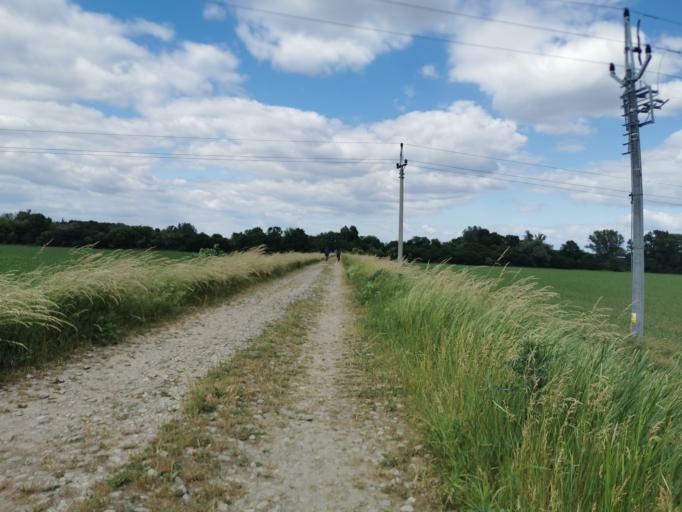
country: CZ
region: South Moravian
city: Rohatec
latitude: 48.8819
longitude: 17.2116
